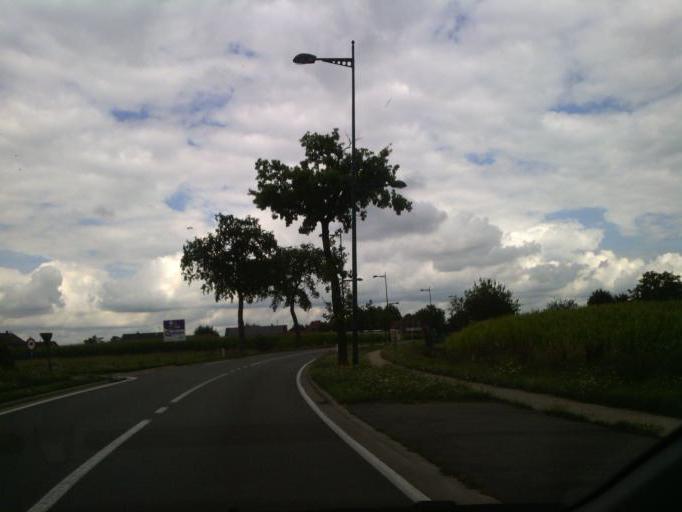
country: BE
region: Flanders
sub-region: Provincie Oost-Vlaanderen
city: Aalter
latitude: 51.0574
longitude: 3.4581
